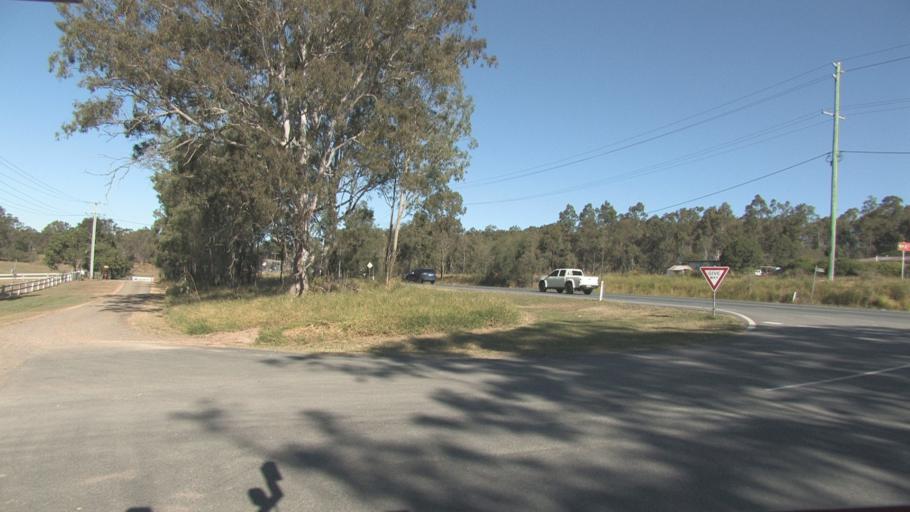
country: AU
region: Queensland
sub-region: Logan
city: North Maclean
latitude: -27.7875
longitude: 153.0138
